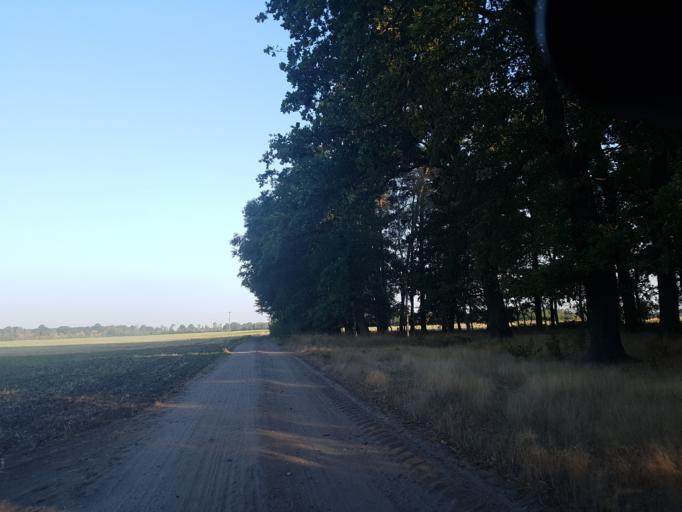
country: DE
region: Brandenburg
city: Herzberg
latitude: 51.6538
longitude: 13.2823
